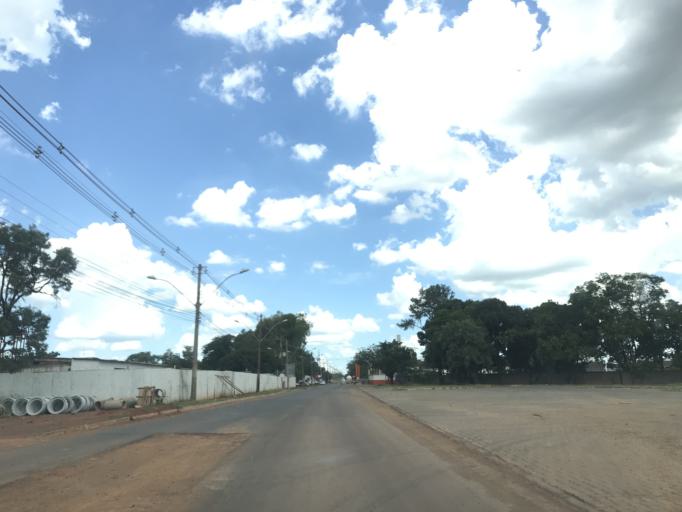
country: BR
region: Federal District
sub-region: Brasilia
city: Brasilia
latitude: -15.7961
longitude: -47.9781
